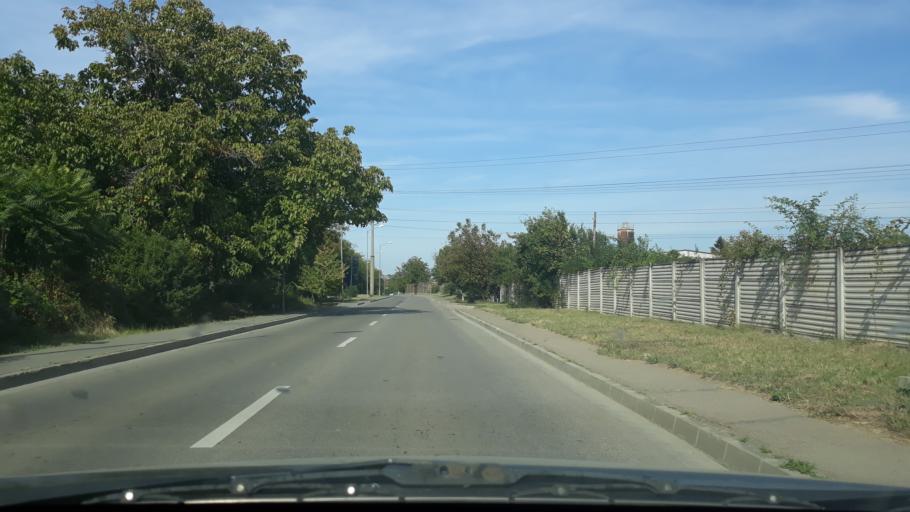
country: RO
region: Bihor
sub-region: Comuna Biharea
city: Oradea
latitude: 47.0365
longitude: 21.9321
